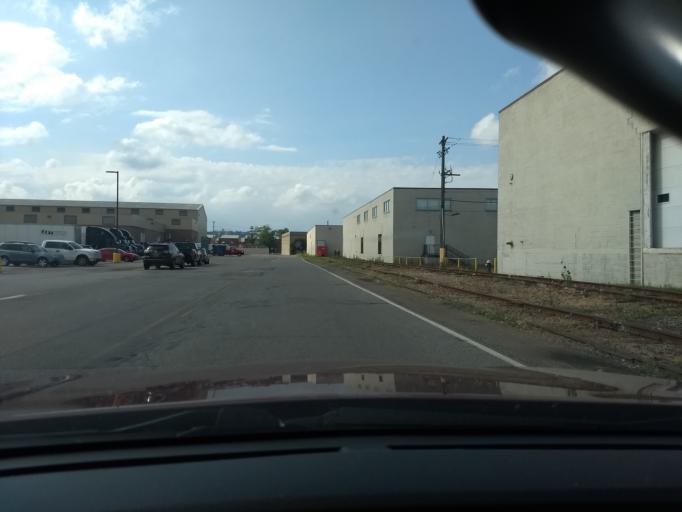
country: US
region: Pennsylvania
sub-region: Allegheny County
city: Leetsdale
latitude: 40.5587
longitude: -80.2112
